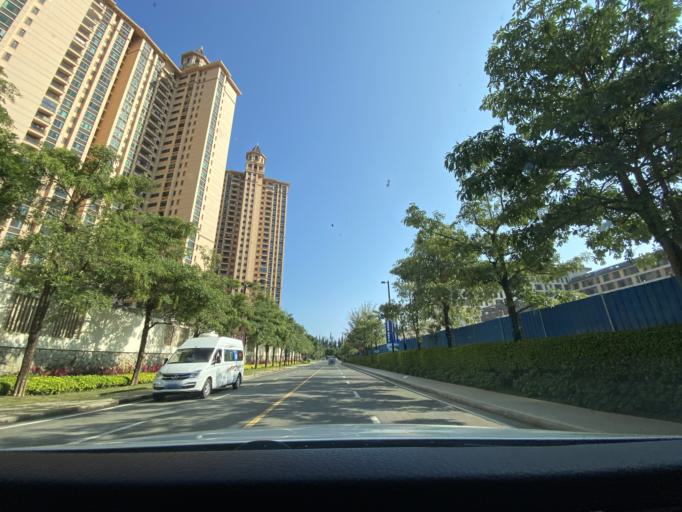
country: CN
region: Hainan
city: Yingzhou
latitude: 18.4120
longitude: 109.8861
